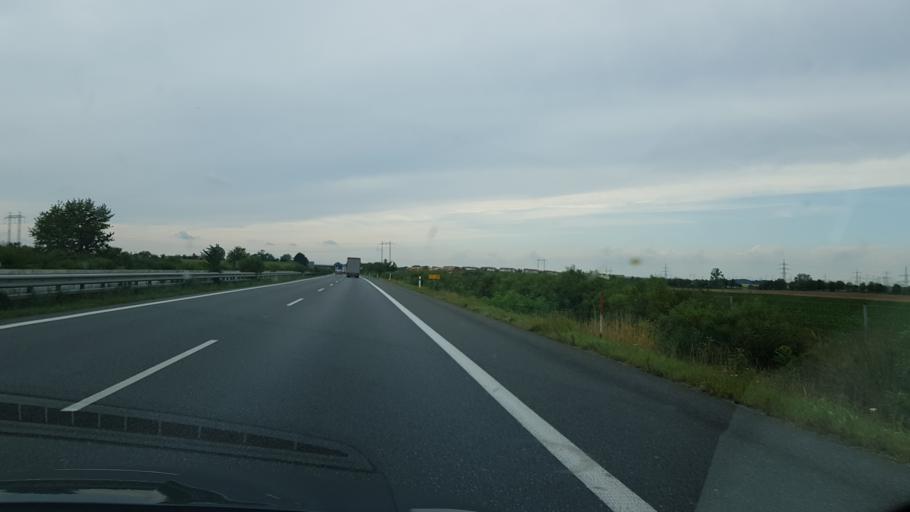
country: CZ
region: Central Bohemia
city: Nehvizdy
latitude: 50.1320
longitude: 14.7591
